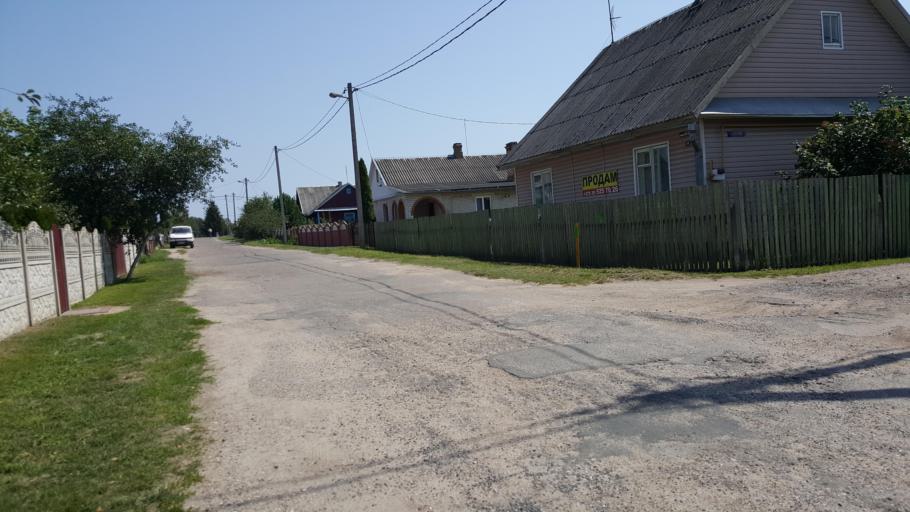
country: BY
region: Brest
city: Zhabinka
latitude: 52.1940
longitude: 24.0139
